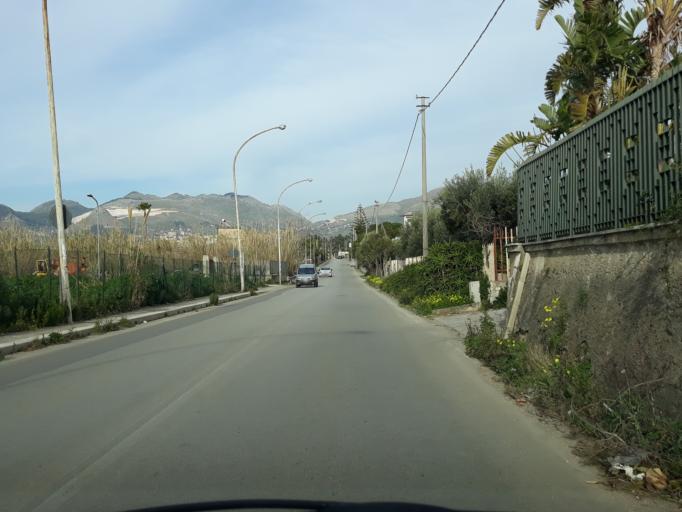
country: IT
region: Sicily
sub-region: Palermo
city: Borgetto
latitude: 38.0584
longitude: 13.1344
